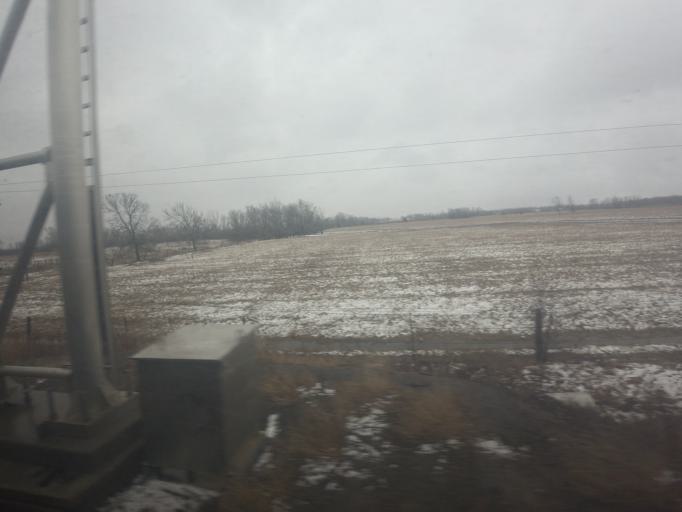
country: CA
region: Ontario
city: Deseronto
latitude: 44.2206
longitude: -77.1445
